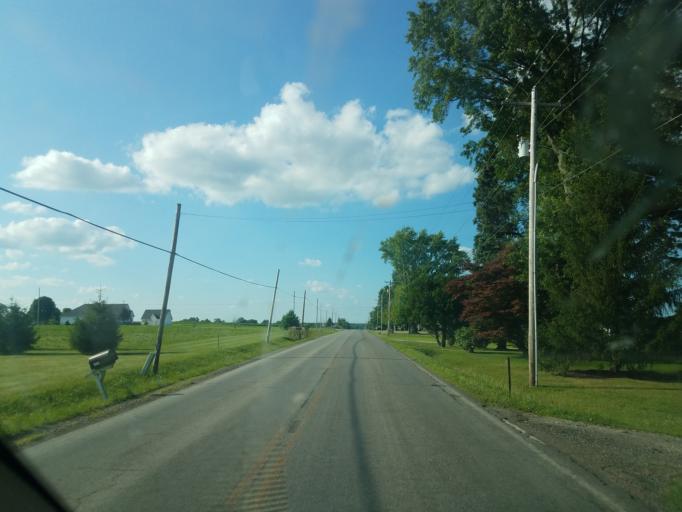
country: US
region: Ohio
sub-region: Wayne County
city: Apple Creek
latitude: 40.7420
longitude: -81.8960
